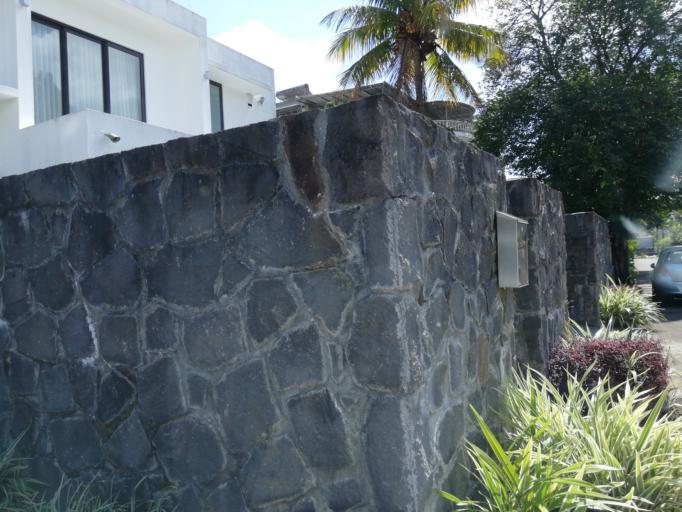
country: MU
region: Moka
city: Saint Pierre
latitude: -20.2257
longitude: 57.5279
